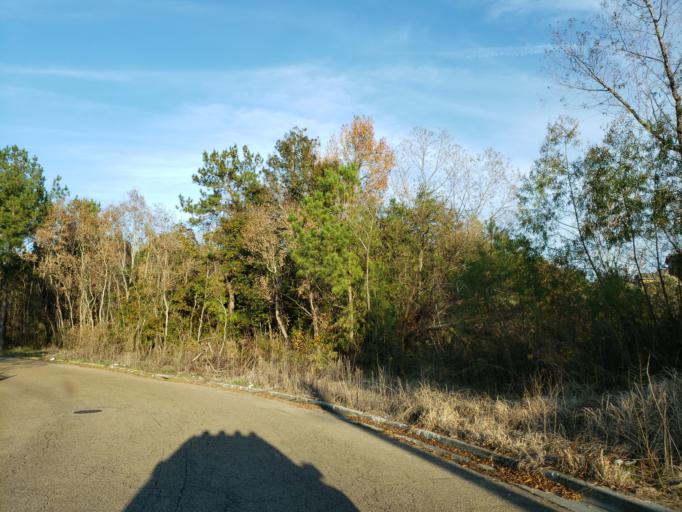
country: US
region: Mississippi
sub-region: Lamar County
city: Arnold Line
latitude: 31.3321
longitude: -89.3499
